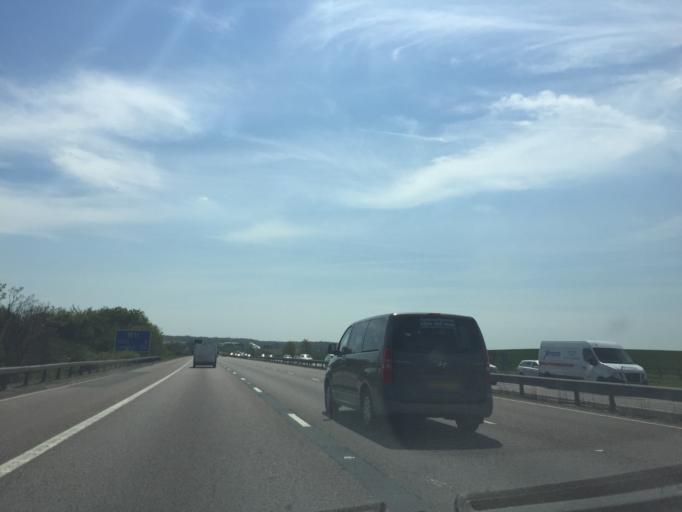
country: GB
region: England
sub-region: Essex
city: Epping
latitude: 51.7353
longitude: 0.1375
